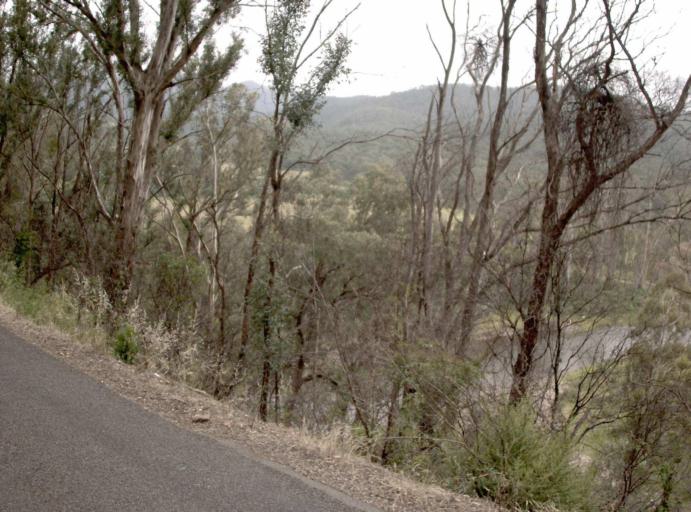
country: AU
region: Victoria
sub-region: Wellington
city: Heyfield
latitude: -37.8094
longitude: 146.6719
